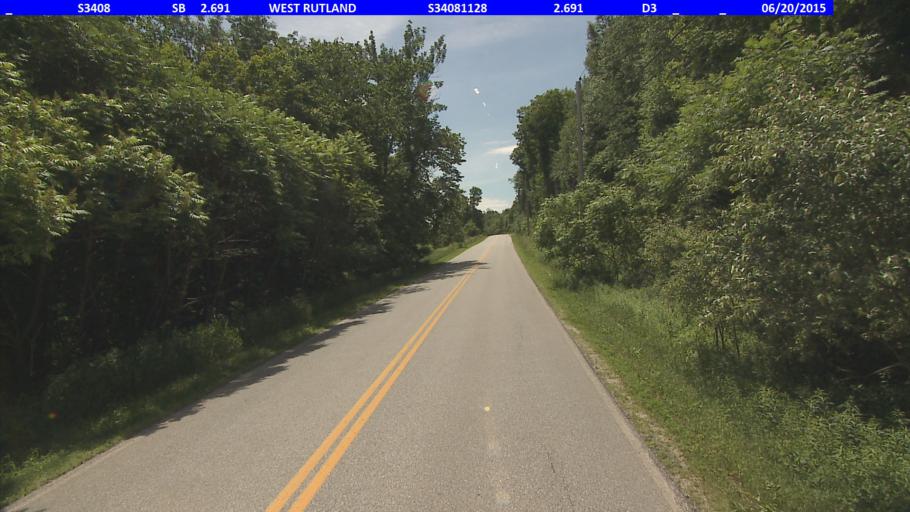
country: US
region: Vermont
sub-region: Rutland County
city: West Rutland
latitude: 43.6477
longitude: -73.0721
